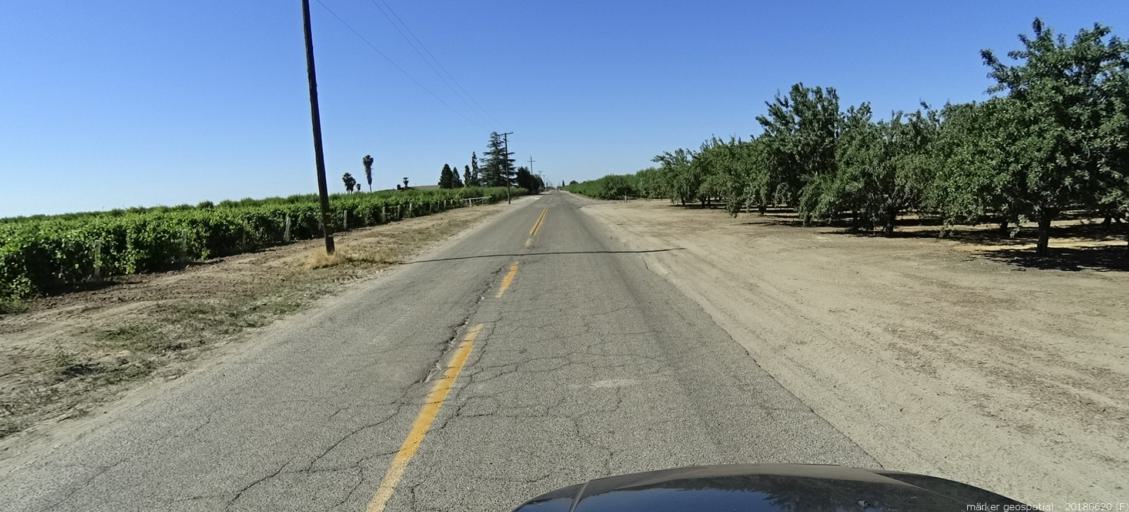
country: US
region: California
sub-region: Madera County
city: Parkwood
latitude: 36.8739
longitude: -120.0375
